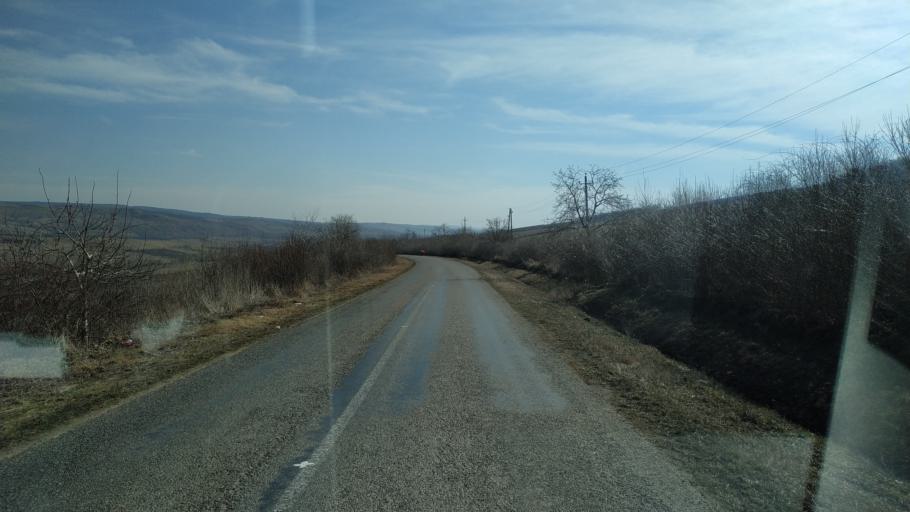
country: MD
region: Nisporeni
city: Nisporeni
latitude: 47.1804
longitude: 28.0795
